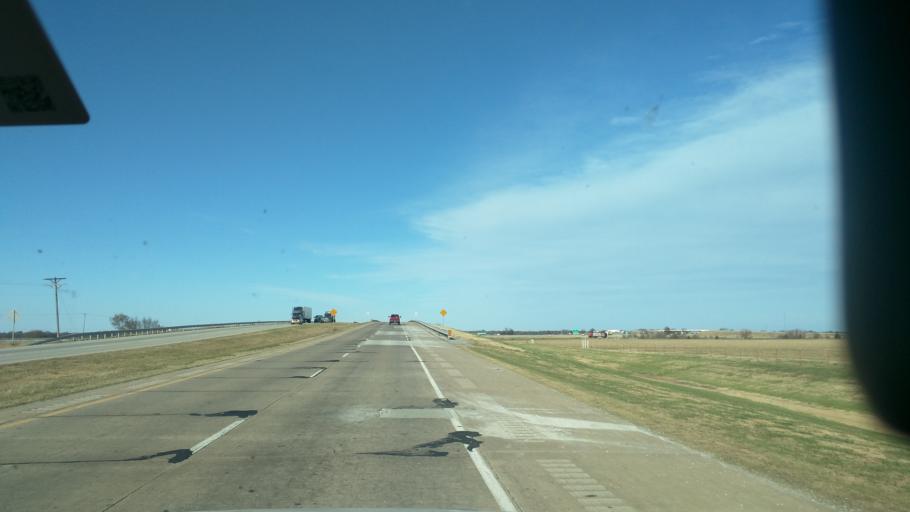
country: US
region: Oklahoma
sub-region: Craig County
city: Vinita
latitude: 36.5545
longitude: -95.2201
